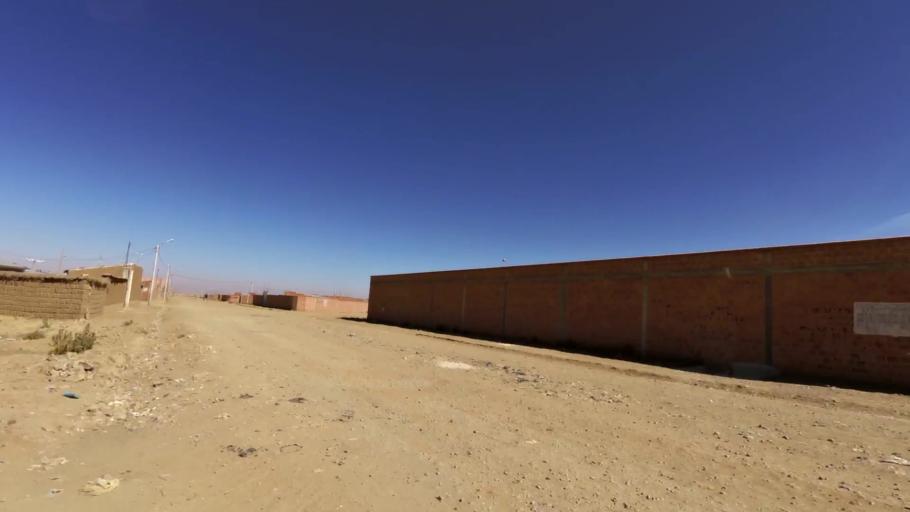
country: BO
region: La Paz
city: La Paz
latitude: -16.6193
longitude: -68.1945
